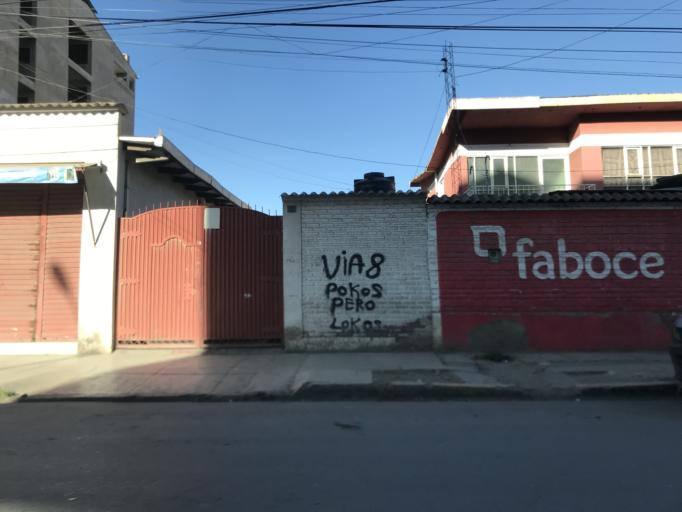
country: BO
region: Cochabamba
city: Cochabamba
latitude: -17.4122
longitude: -66.1511
